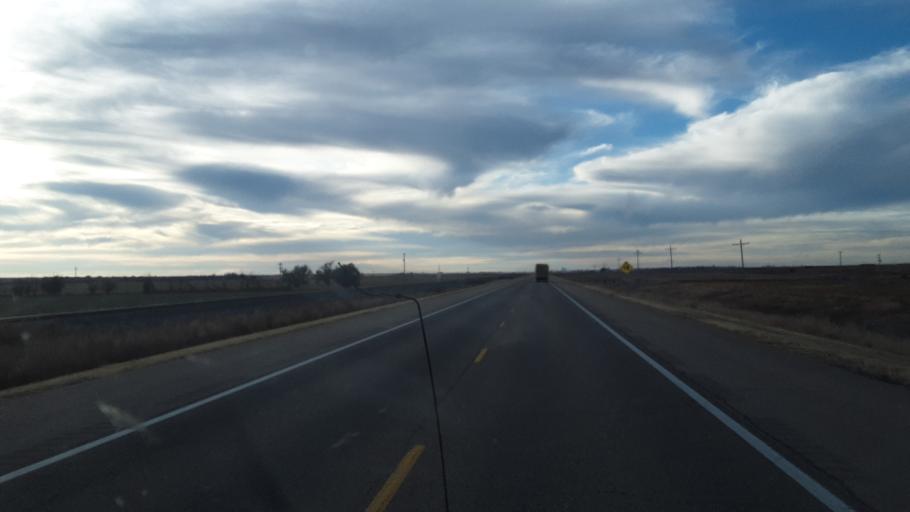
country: US
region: Kansas
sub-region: Hamilton County
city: Syracuse
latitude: 37.9648
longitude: -101.6847
